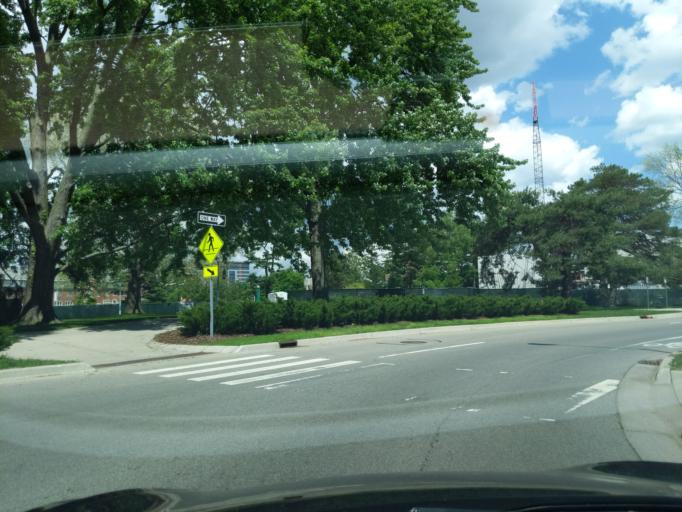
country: US
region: Michigan
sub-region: Ingham County
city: East Lansing
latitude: 42.7323
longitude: -84.4864
